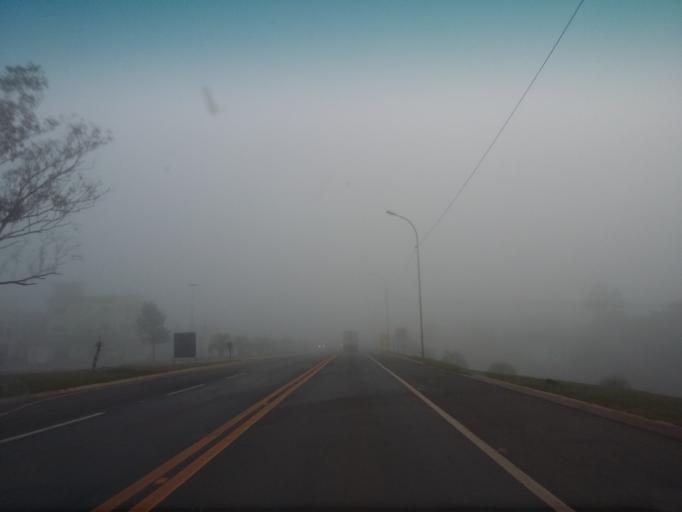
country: BR
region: Santa Catarina
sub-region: Curitibanos
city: Curitibanos
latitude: -27.2695
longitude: -50.4411
